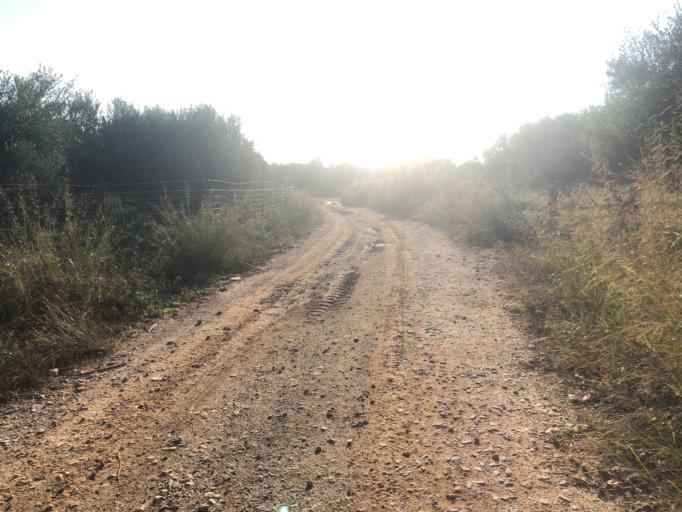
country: GR
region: Crete
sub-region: Nomos Chanias
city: Georgioupolis
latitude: 35.3419
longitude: 24.2868
